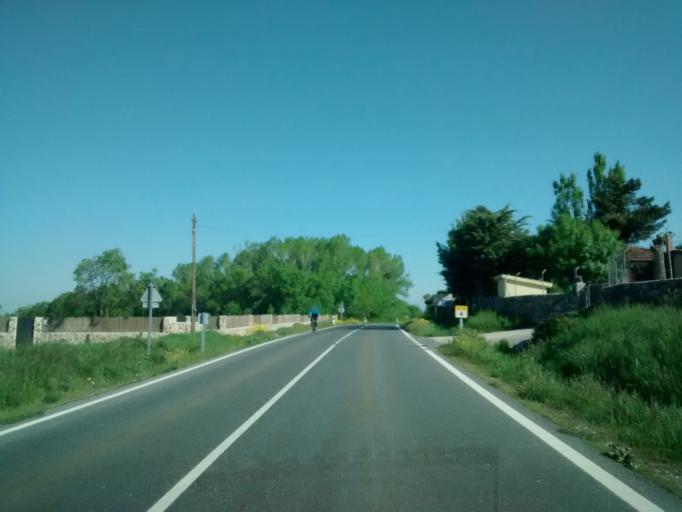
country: ES
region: Castille and Leon
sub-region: Provincia de Segovia
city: Palazuelos de Eresma
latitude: 40.9287
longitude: -4.0310
